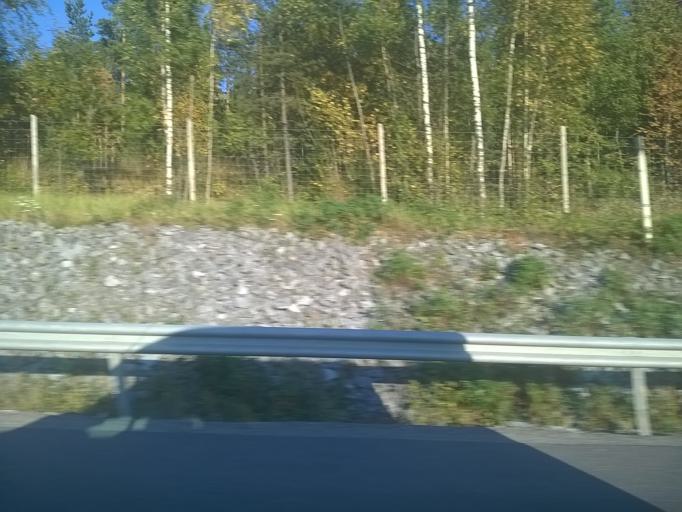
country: FI
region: Pirkanmaa
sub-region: Tampere
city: Tampere
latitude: 61.4458
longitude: 23.7643
